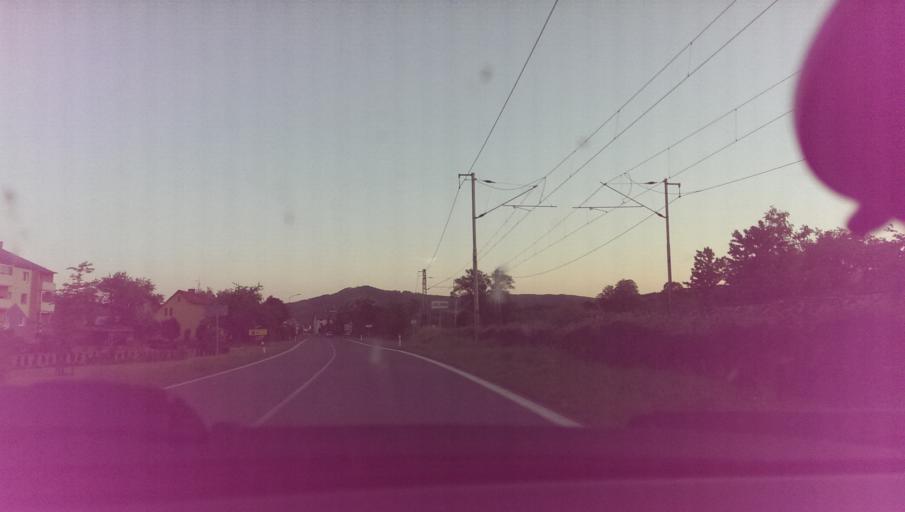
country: CZ
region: Zlin
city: Jablunka
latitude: 49.3911
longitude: 17.9500
